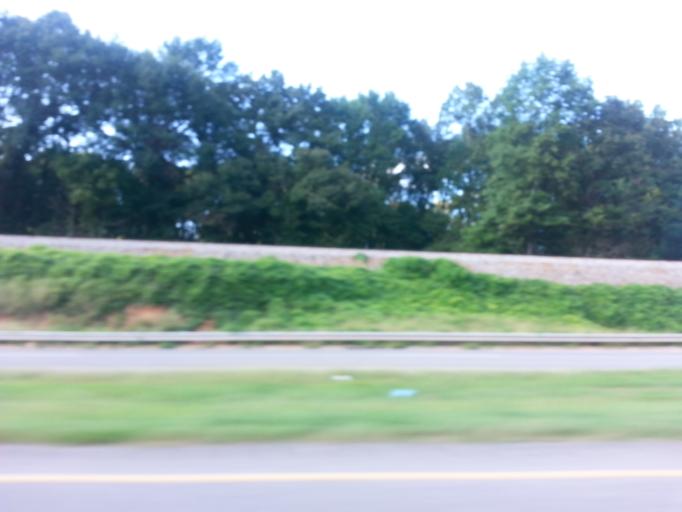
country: US
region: Alabama
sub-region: Colbert County
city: Tuscumbia
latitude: 34.7096
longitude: -87.7523
